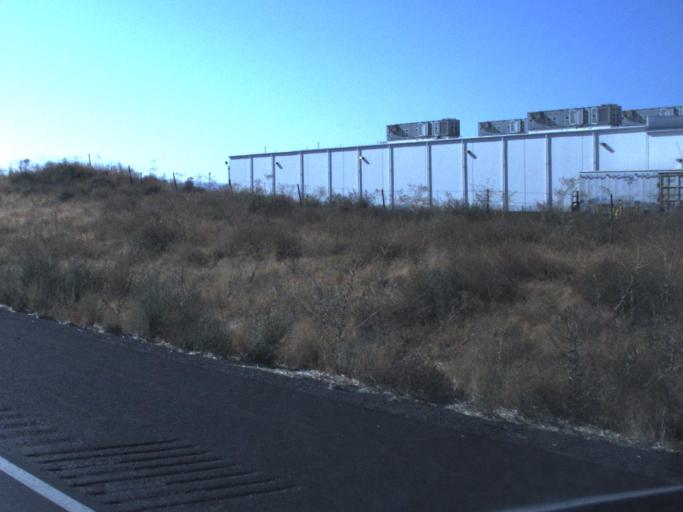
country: US
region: Washington
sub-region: Franklin County
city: Pasco
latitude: 46.2757
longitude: -119.0907
